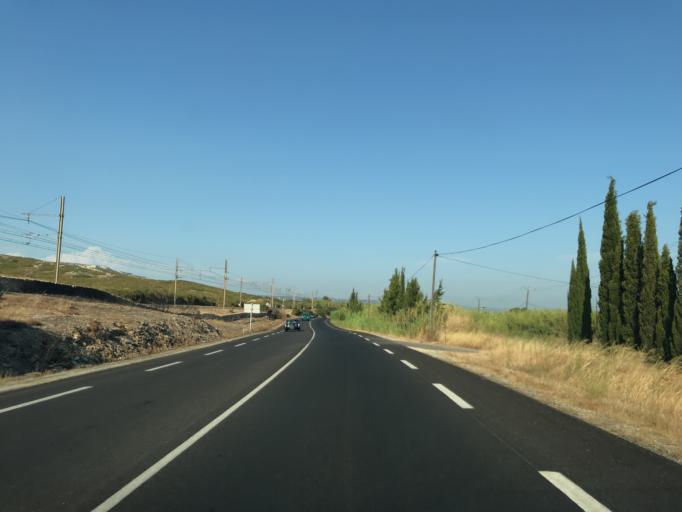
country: FR
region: Provence-Alpes-Cote d'Azur
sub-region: Departement des Bouches-du-Rhone
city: Cornillon-Confoux
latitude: 43.5310
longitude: 5.1038
